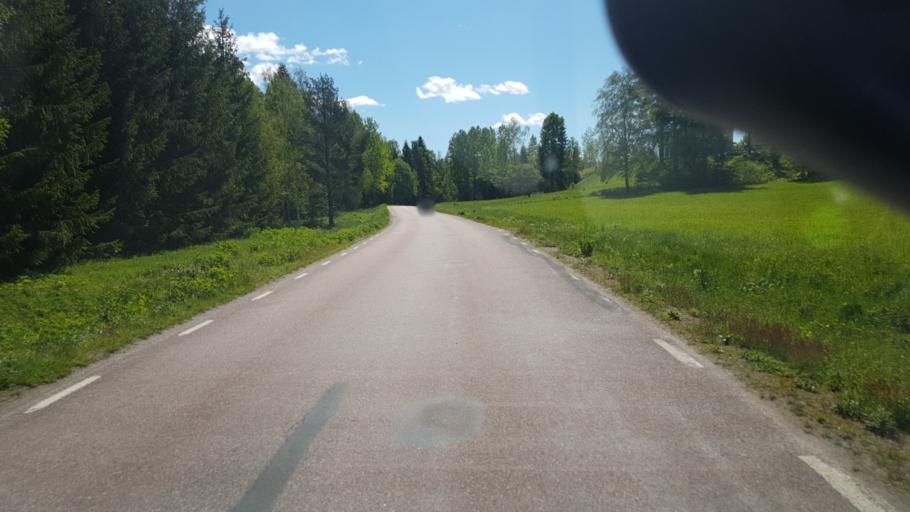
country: SE
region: Vaermland
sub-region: Grums Kommun
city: Slottsbron
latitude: 59.4600
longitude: 12.8775
